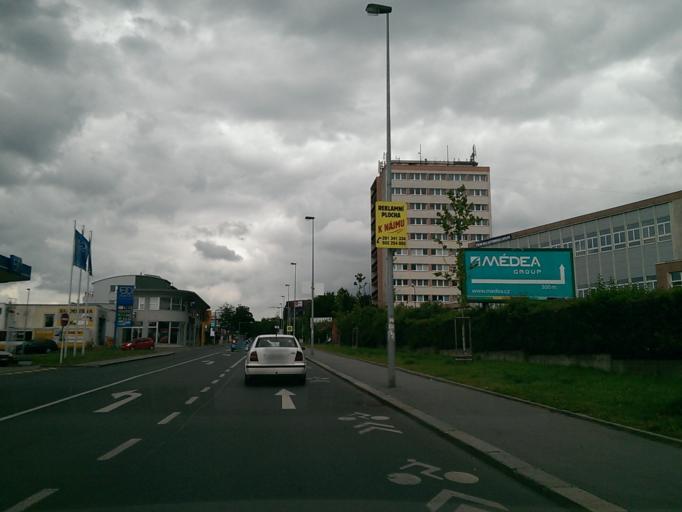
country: CZ
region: Praha
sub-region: Praha 4
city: Hodkovicky
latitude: 50.0316
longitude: 14.4243
